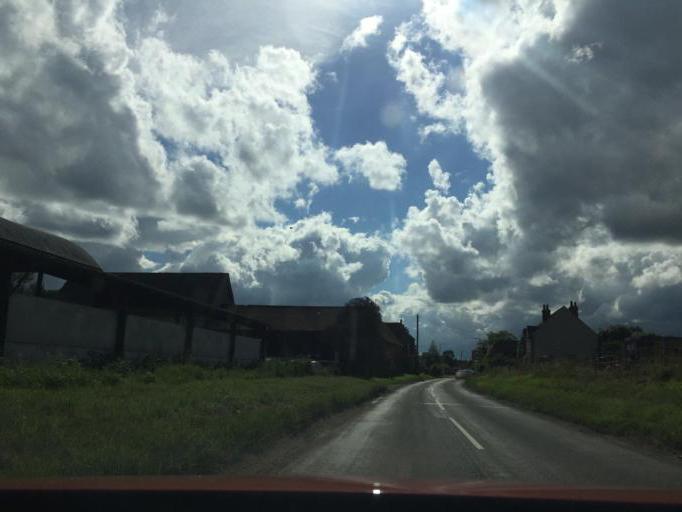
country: GB
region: England
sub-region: Hertfordshire
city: Wheathampstead
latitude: 51.8518
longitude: -0.2866
